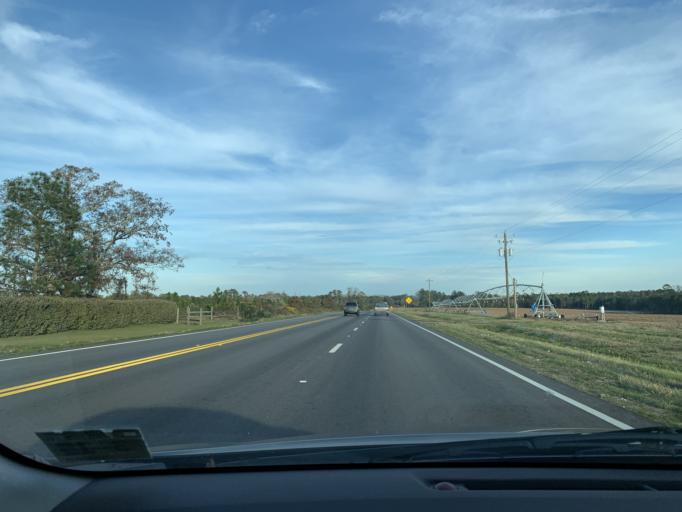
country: US
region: Georgia
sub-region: Irwin County
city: Ocilla
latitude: 31.5949
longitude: -83.1842
